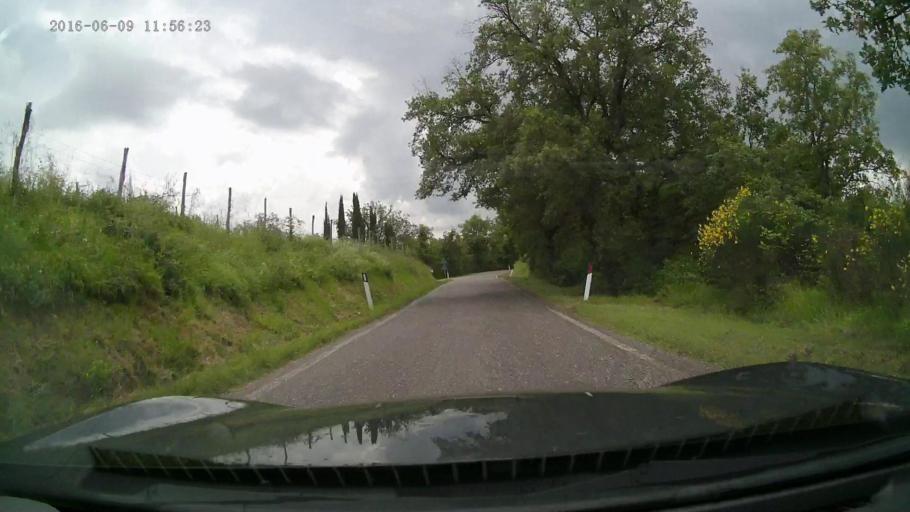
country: IT
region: Tuscany
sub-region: Province of Florence
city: Panzano in Chianti
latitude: 43.5609
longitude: 11.2963
